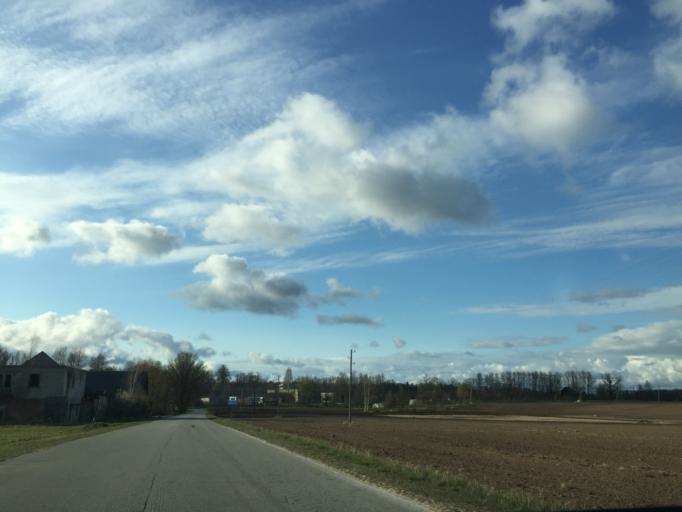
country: LV
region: Burtnieki
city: Matisi
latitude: 57.6333
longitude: 25.0527
